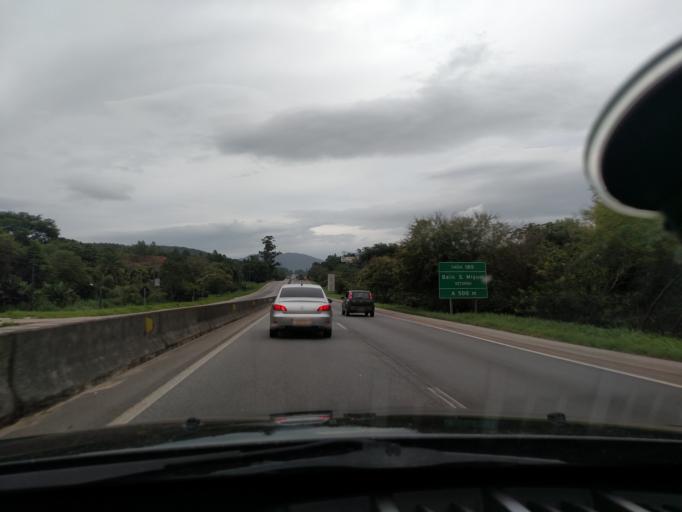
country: BR
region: Santa Catarina
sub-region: Biguacu
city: Biguacu
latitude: -27.4647
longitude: -48.6420
